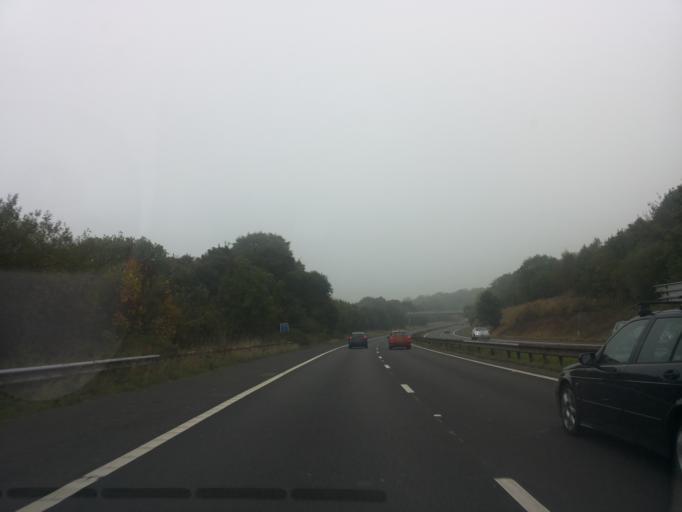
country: GB
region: England
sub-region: Borough of Bury
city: Ramsbottom
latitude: 53.6381
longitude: -2.3068
